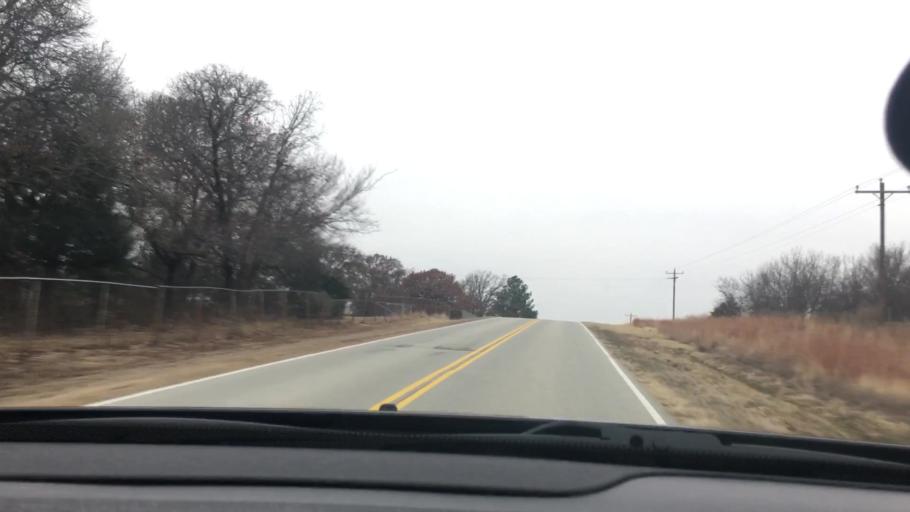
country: US
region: Oklahoma
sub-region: Coal County
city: Coalgate
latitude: 34.5055
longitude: -96.3375
